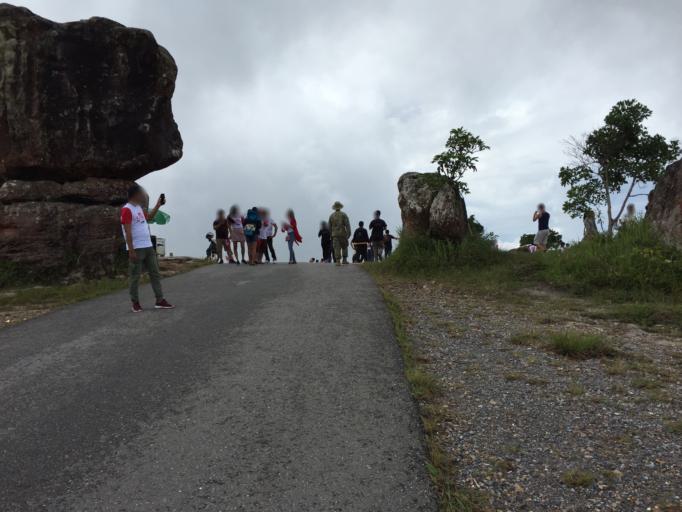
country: KH
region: Kampot
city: Kampot
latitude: 10.6211
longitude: 104.0759
